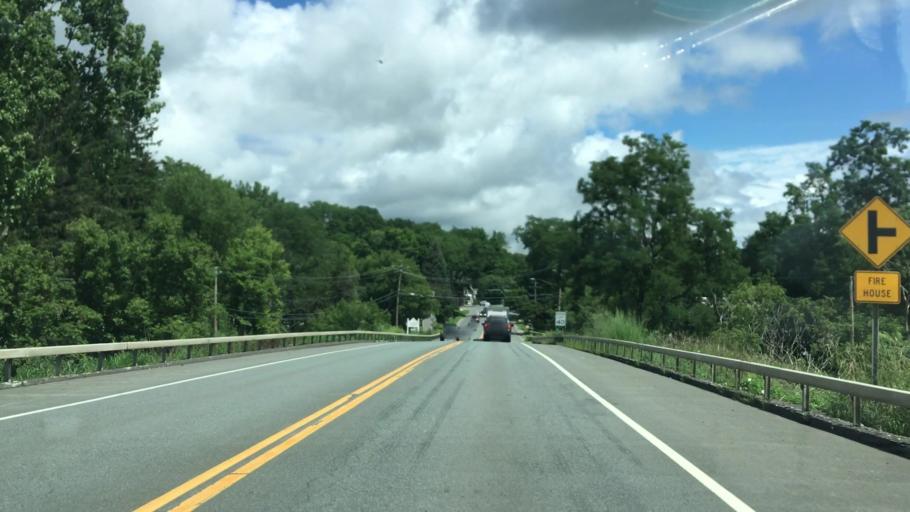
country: US
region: New York
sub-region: Rensselaer County
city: Hoosick Falls
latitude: 42.8615
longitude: -73.3309
